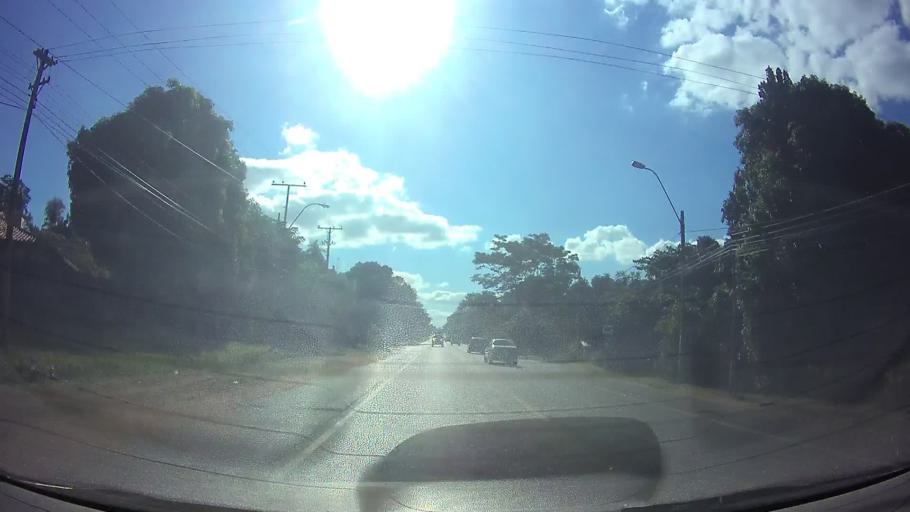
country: PY
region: Cordillera
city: Caacupe
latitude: -25.3895
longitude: -57.1630
